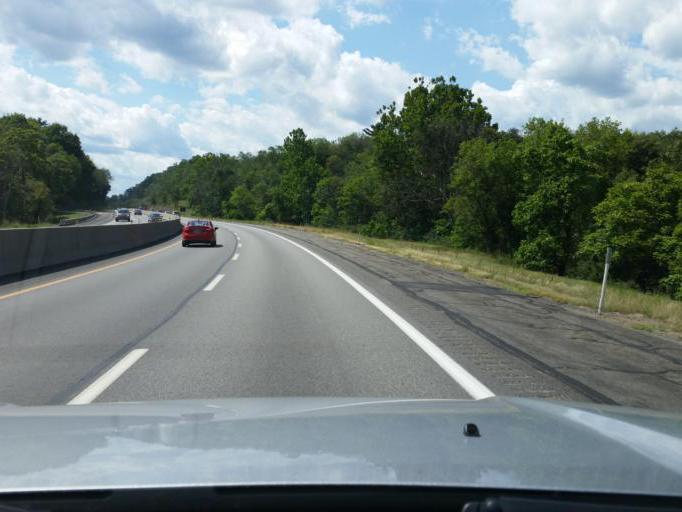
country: US
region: Pennsylvania
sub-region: Bedford County
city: Earlston
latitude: 39.9989
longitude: -78.3385
